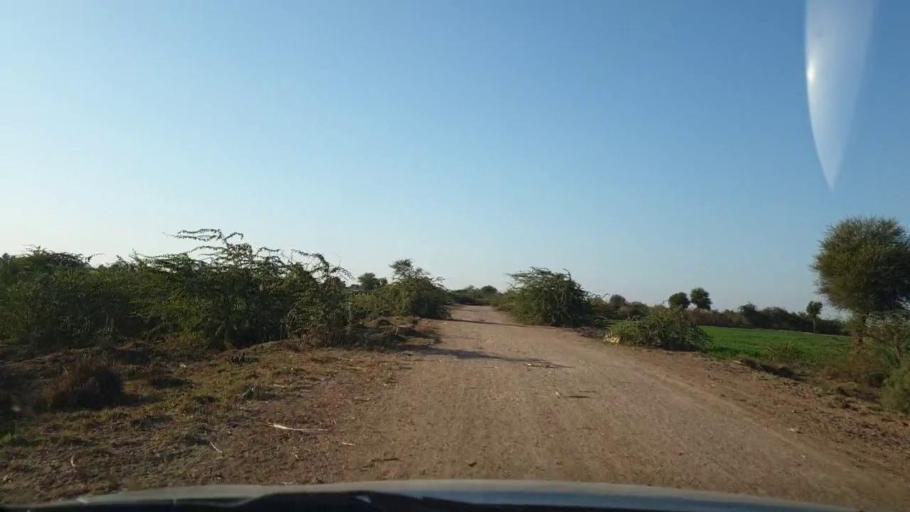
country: PK
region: Sindh
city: Jhol
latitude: 25.8993
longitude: 68.9262
